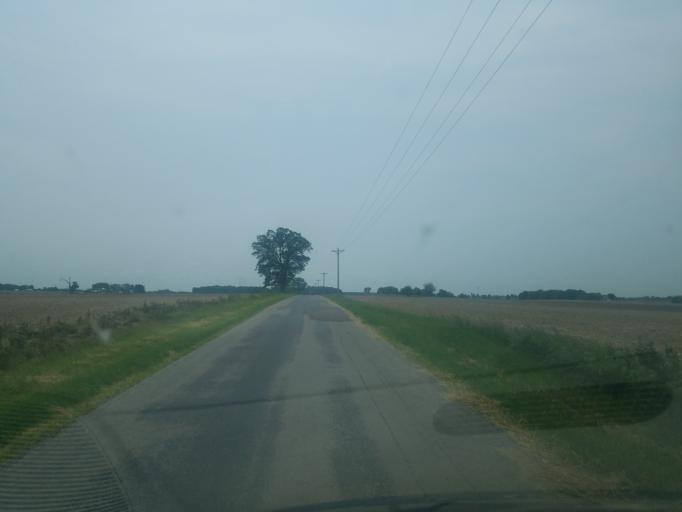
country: US
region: Ohio
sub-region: Marion County
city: Marion
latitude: 40.6538
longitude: -83.1979
